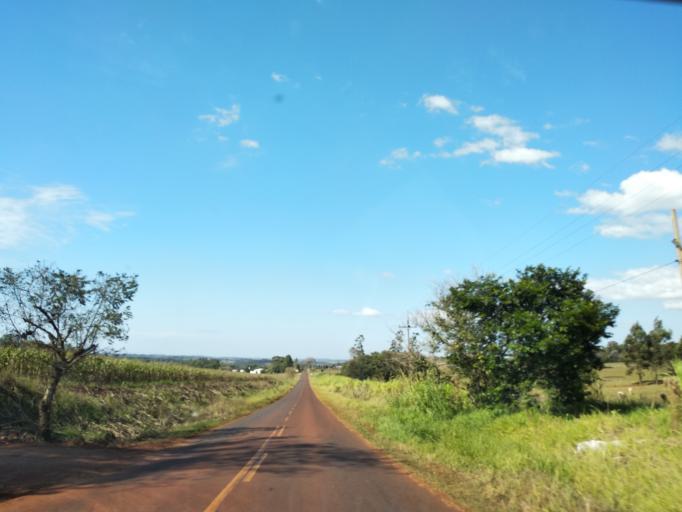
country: PY
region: Itapua
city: Hohenau
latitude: -27.0766
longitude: -55.7128
